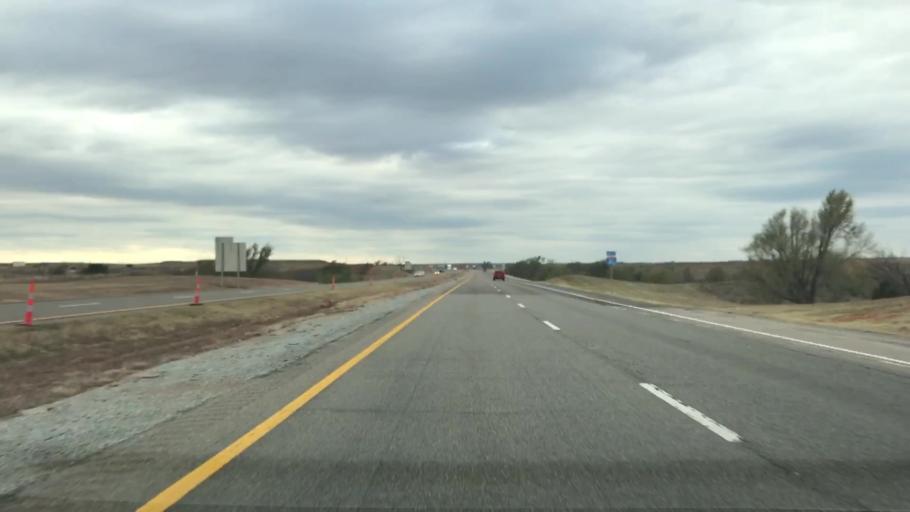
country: US
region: Oklahoma
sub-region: Washita County
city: Burns Flat
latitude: 35.4416
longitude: -99.1782
